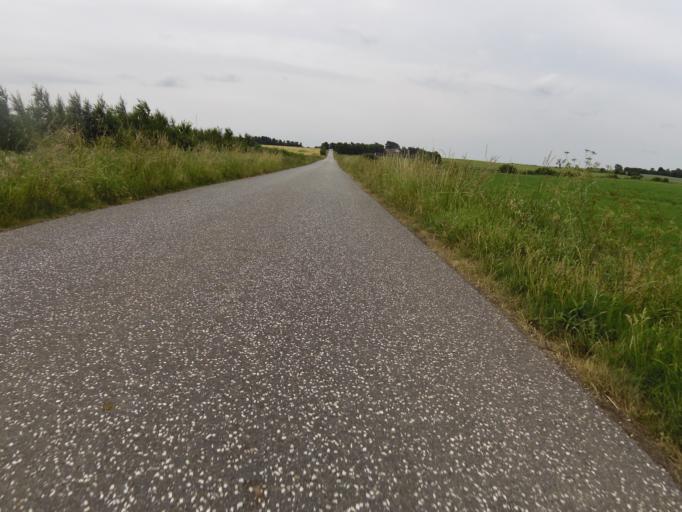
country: DK
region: Central Jutland
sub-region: Holstebro Kommune
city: Holstebro
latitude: 56.4161
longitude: 8.6723
